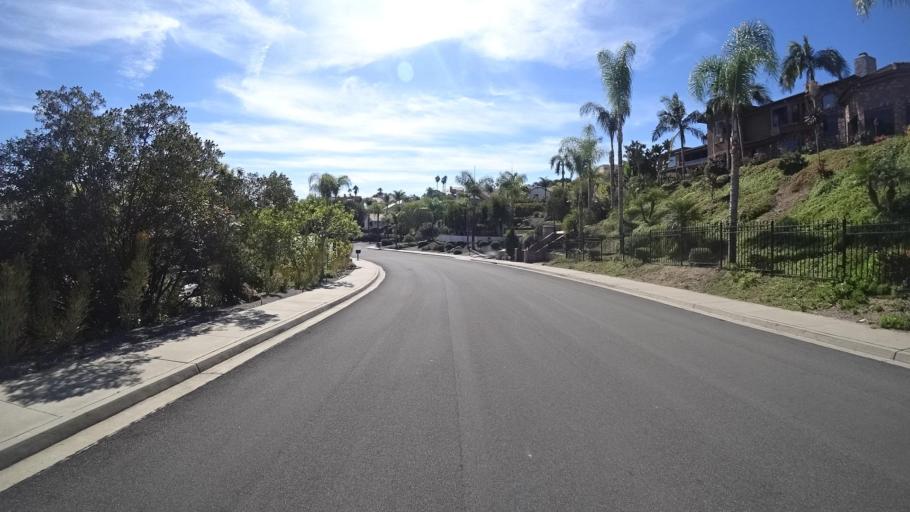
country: US
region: California
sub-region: San Diego County
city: Rancho San Diego
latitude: 32.7571
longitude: -116.9482
